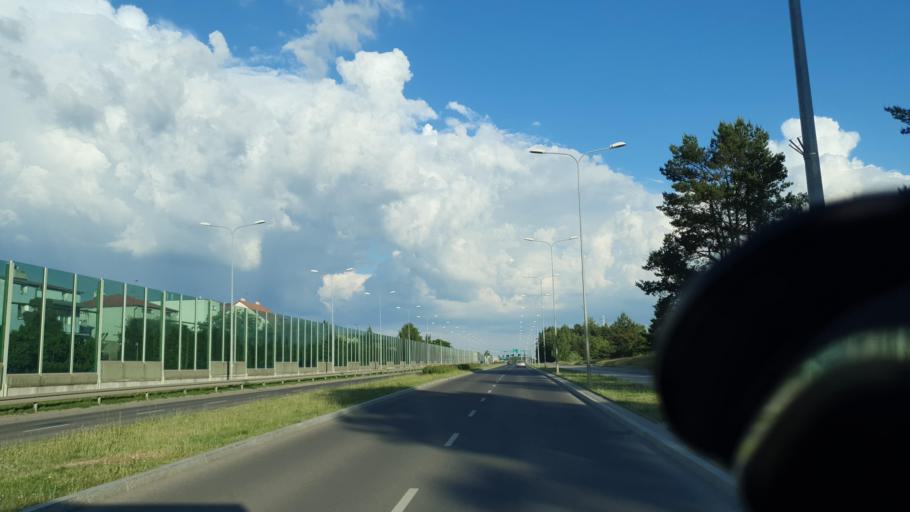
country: PL
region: Podlasie
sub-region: Powiat bialostocki
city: Wasilkow
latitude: 53.1638
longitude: 23.1938
